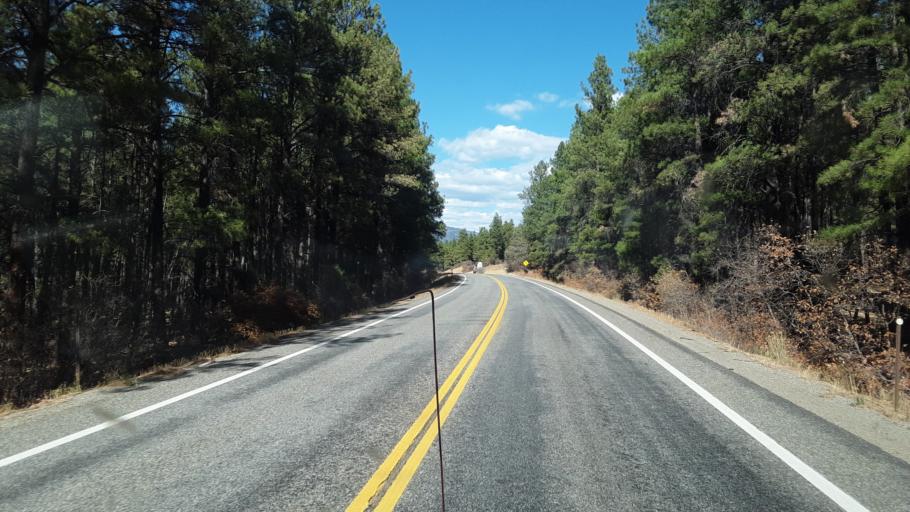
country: US
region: Colorado
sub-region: La Plata County
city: Bayfield
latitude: 37.2179
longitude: -107.3390
